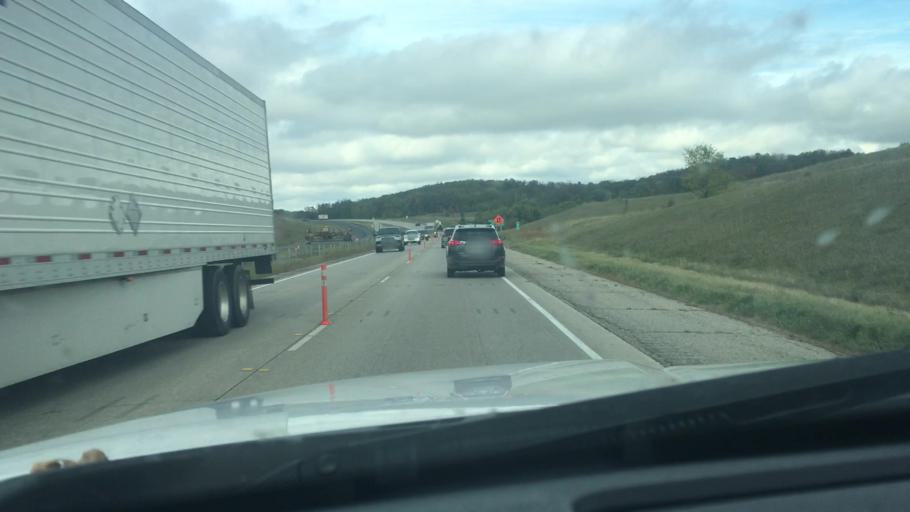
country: US
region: Minnesota
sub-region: Douglas County
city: Alexandria
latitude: 45.8920
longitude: -95.5109
